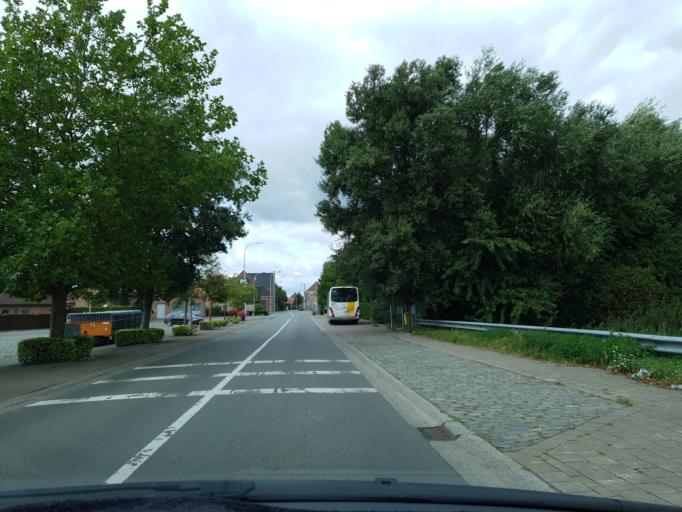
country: BE
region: Wallonia
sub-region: Province du Hainaut
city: Pecq
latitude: 50.7186
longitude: 3.3552
